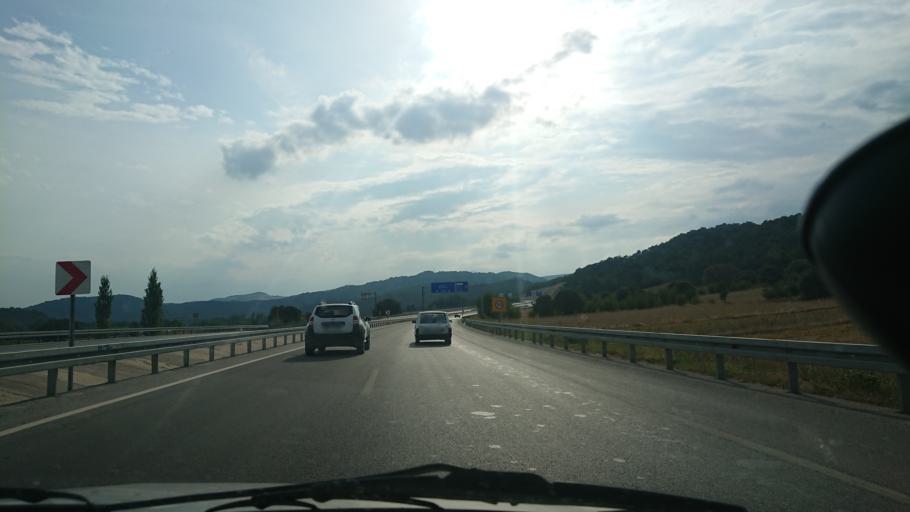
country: TR
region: Kuetahya
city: Gediz
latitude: 38.9364
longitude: 29.3141
